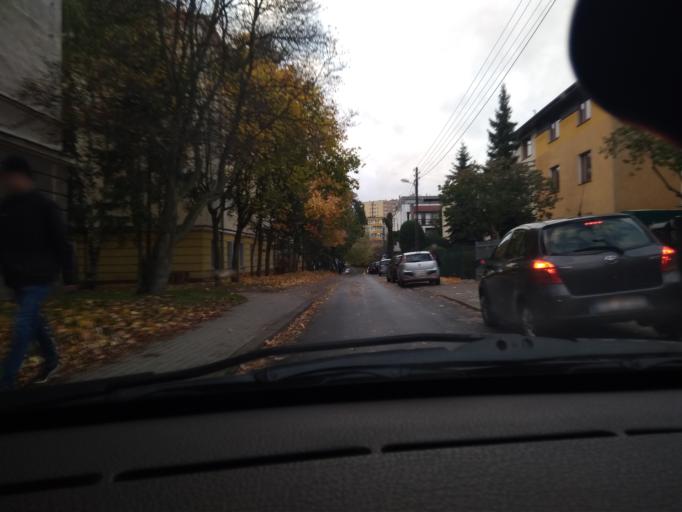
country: PL
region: Greater Poland Voivodeship
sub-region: Poznan
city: Poznan
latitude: 52.4268
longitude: 16.9259
